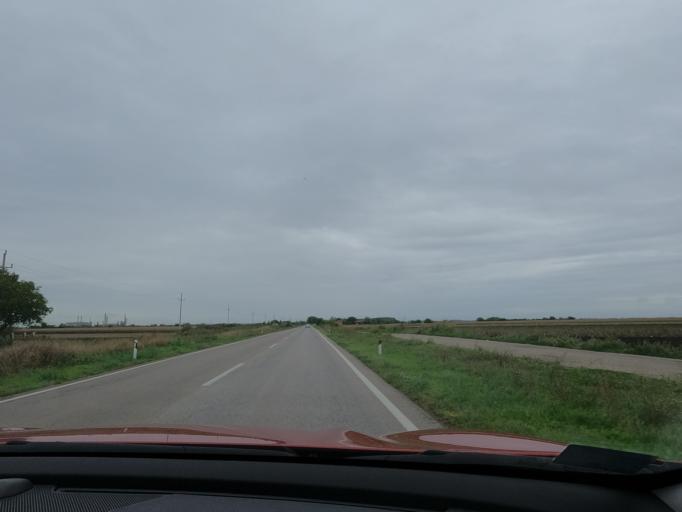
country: RS
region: Autonomna Pokrajina Vojvodina
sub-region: Severnobanatski Okrug
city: Kikinda
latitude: 45.7753
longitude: 20.4269
